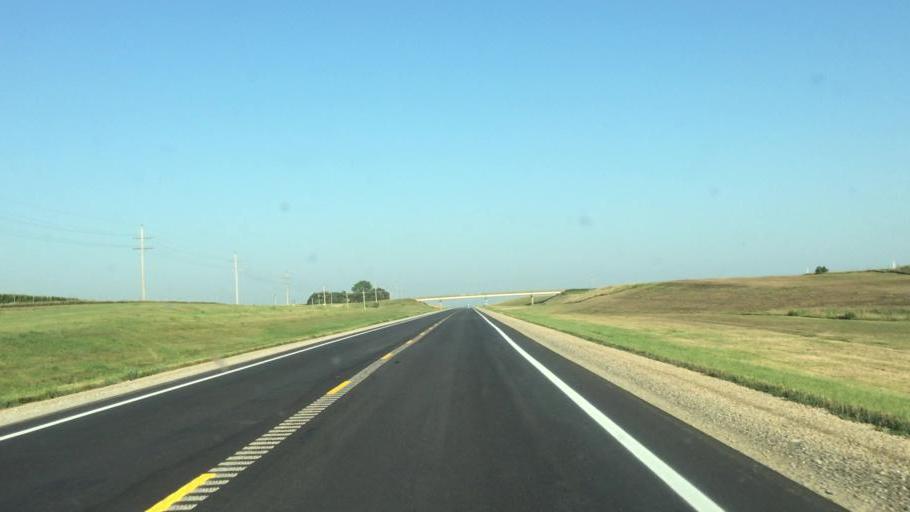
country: US
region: Kansas
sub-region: Brown County
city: Hiawatha
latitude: 39.8420
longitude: -95.4455
